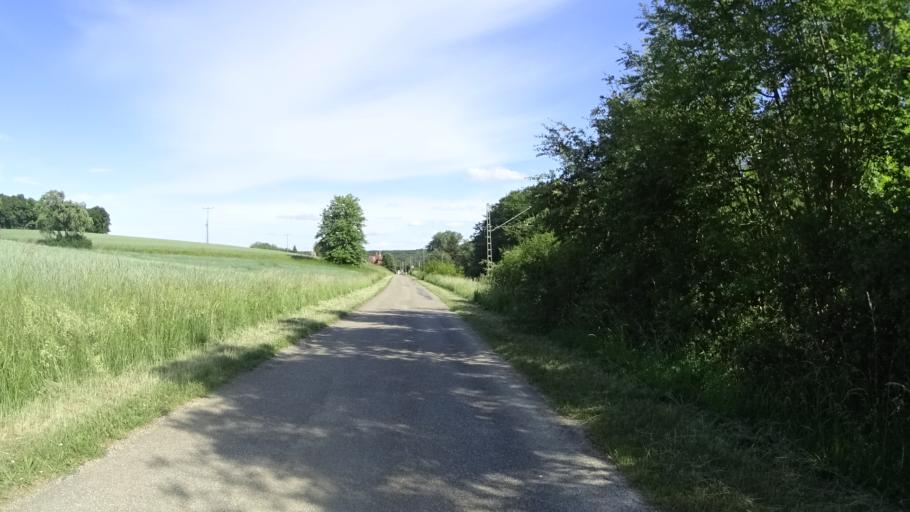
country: DE
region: Baden-Wuerttemberg
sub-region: Regierungsbezirk Stuttgart
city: Buch am Ahorn
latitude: 49.5222
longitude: 9.5823
